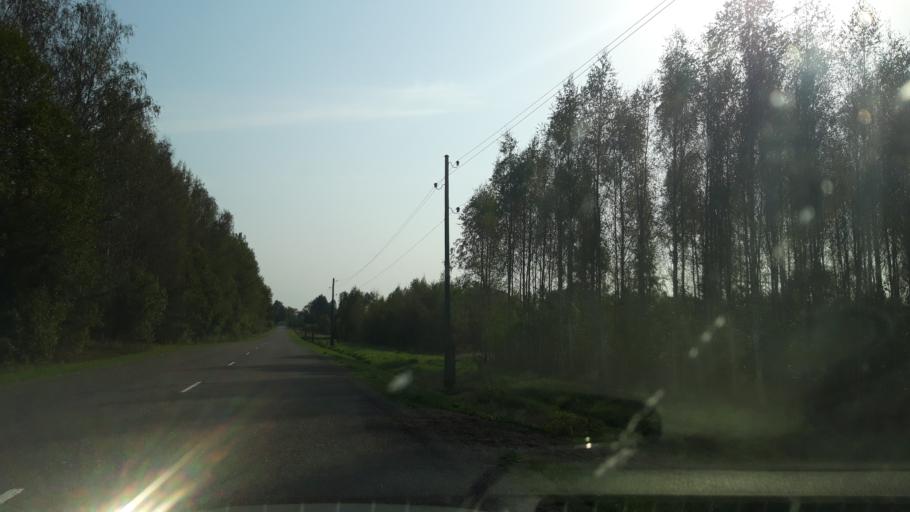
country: LV
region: Burtnieki
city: Matisi
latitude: 57.6316
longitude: 25.2615
